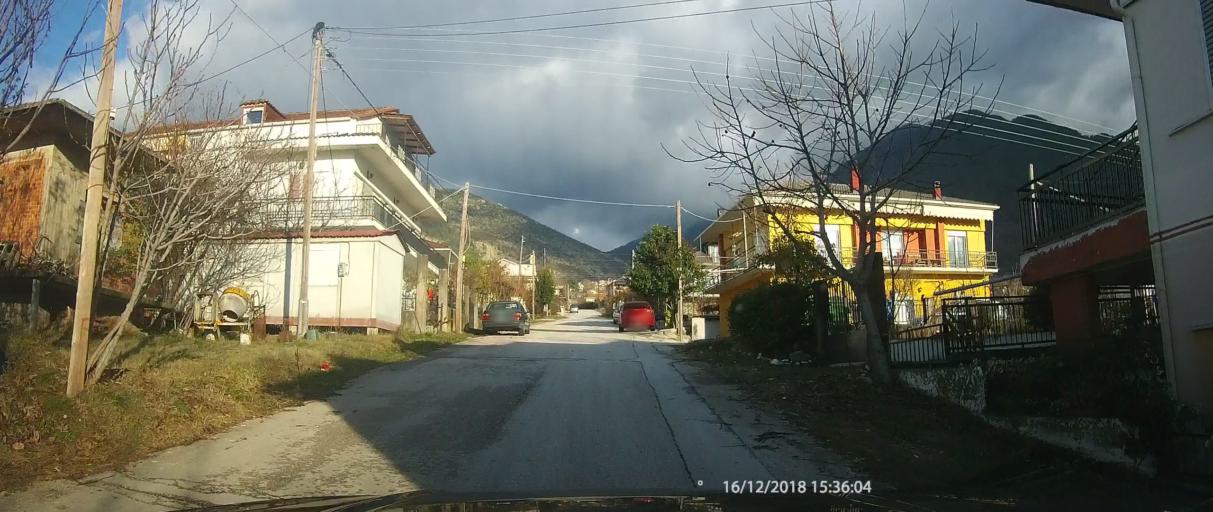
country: GR
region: Epirus
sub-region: Nomos Ioanninon
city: Konitsa
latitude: 40.0467
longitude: 20.7394
